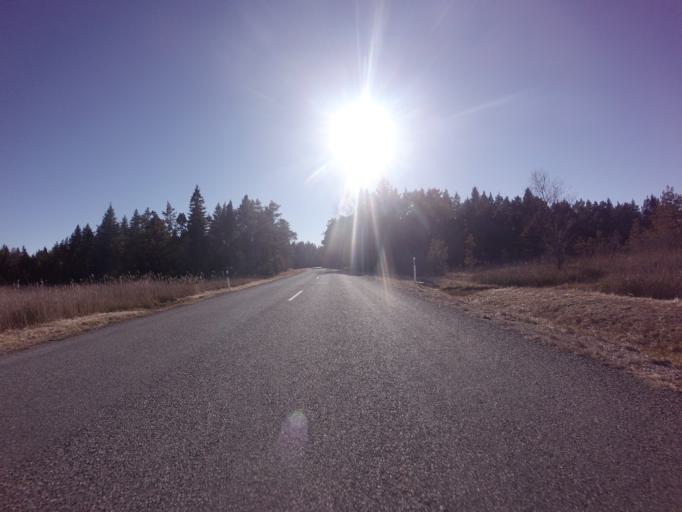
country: EE
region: Saare
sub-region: Kuressaare linn
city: Kuressaare
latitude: 58.5059
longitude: 22.3126
